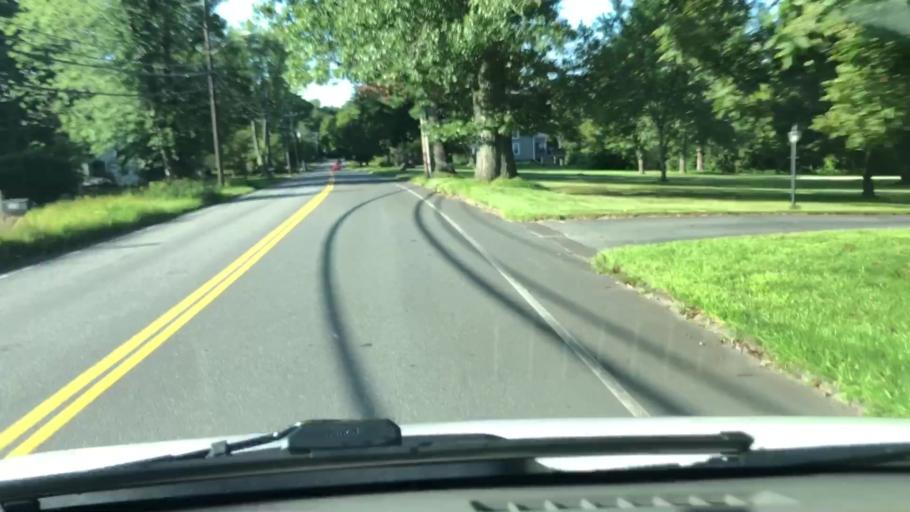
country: US
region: Massachusetts
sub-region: Franklin County
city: Greenfield
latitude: 42.6157
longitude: -72.6118
